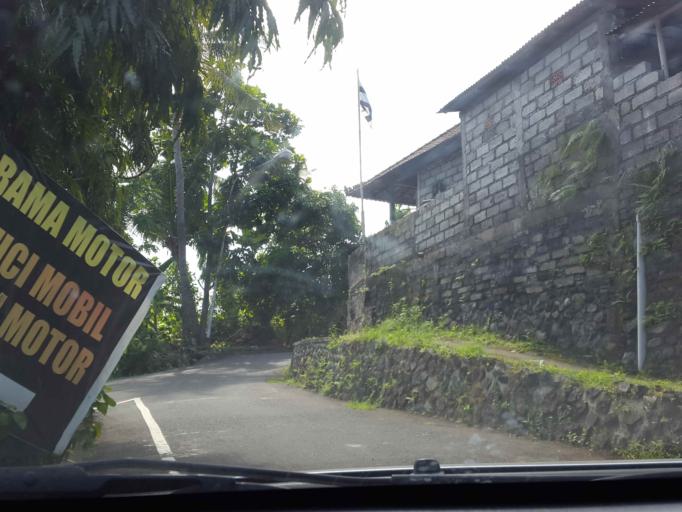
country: ID
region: Bali
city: Semarapura
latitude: -8.5428
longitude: 115.4072
